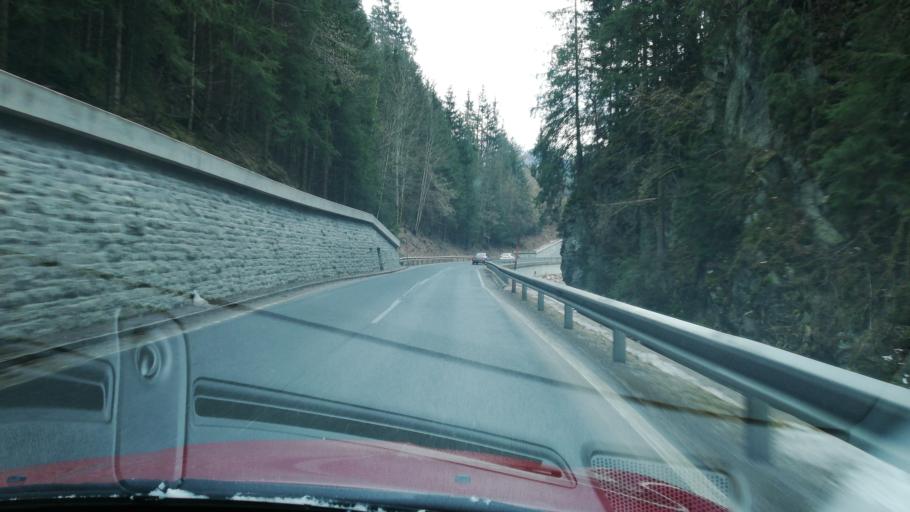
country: AT
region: Styria
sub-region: Politischer Bezirk Liezen
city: Irdning
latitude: 47.4843
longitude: 14.1129
